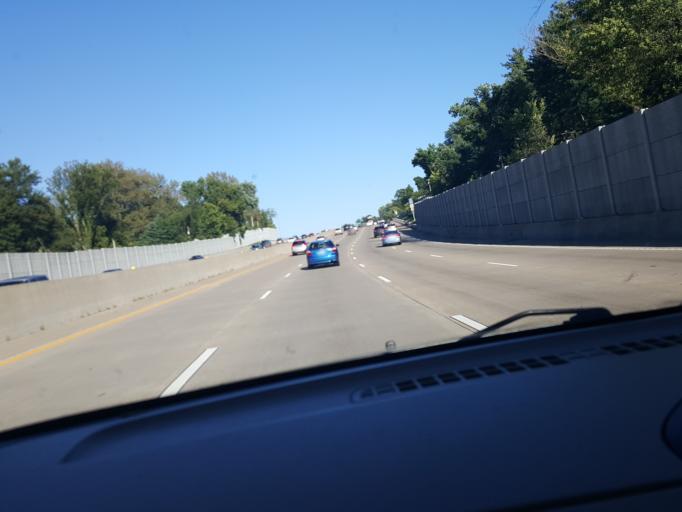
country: US
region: Missouri
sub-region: Saint Louis County
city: Ladue
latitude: 38.6310
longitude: -90.3709
